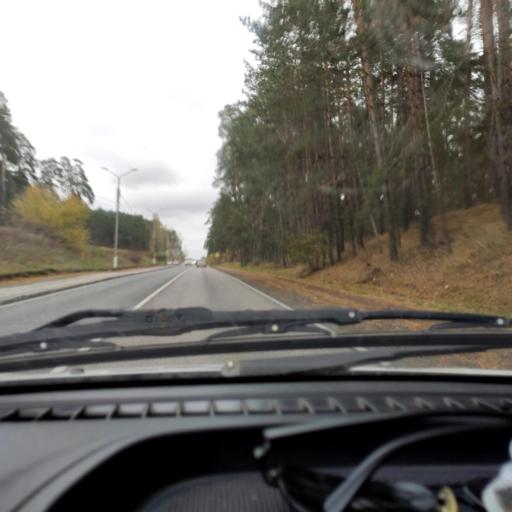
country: RU
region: Samara
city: Tol'yatti
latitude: 53.4762
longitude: 49.3362
